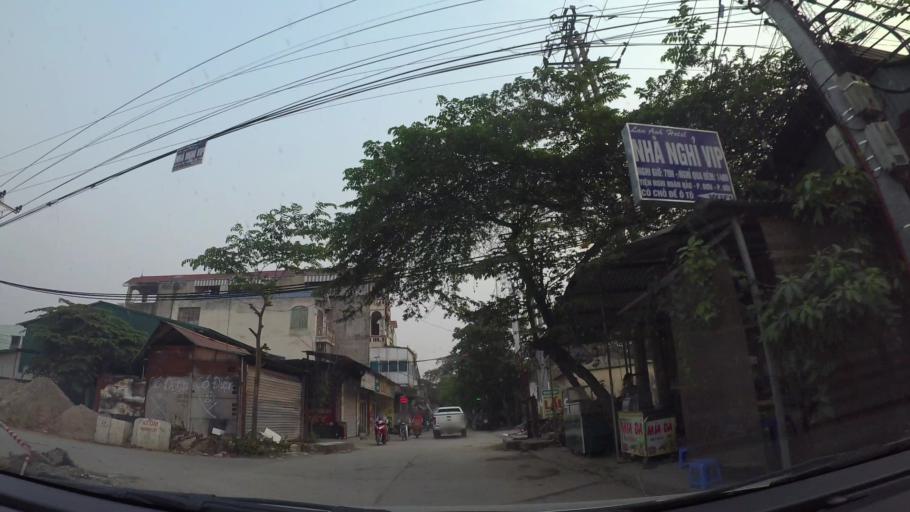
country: VN
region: Ha Noi
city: Ha Dong
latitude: 20.9964
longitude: 105.7297
